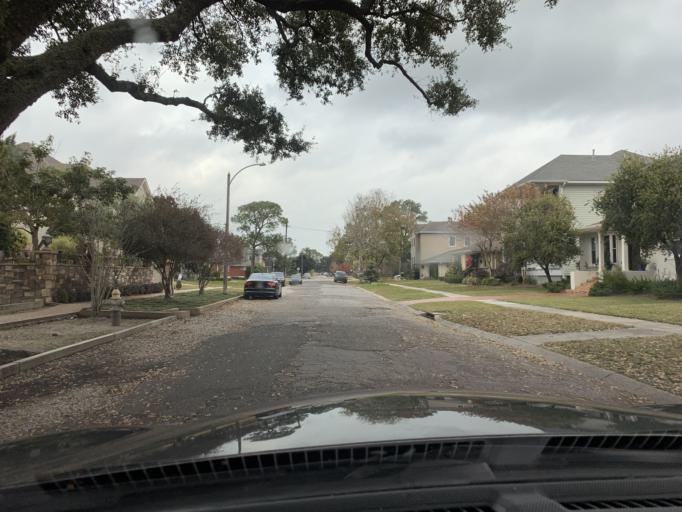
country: US
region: Louisiana
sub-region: Jefferson Parish
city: Metairie
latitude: 30.0091
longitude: -90.1032
